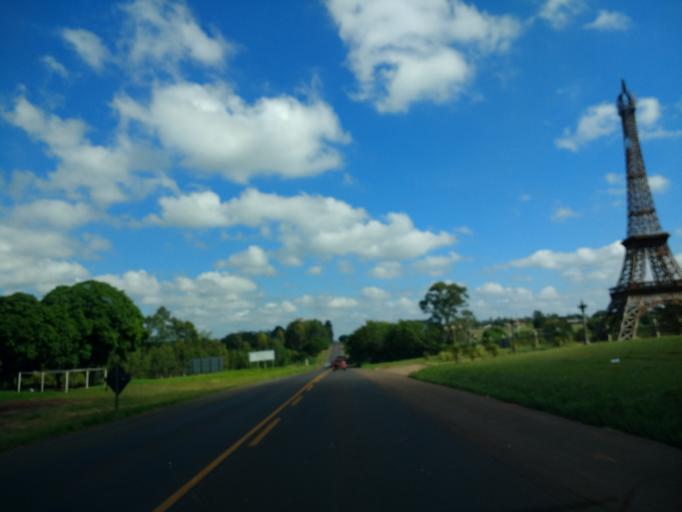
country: BR
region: Parana
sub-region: Umuarama
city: Umuarama
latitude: -23.8340
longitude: -53.3564
